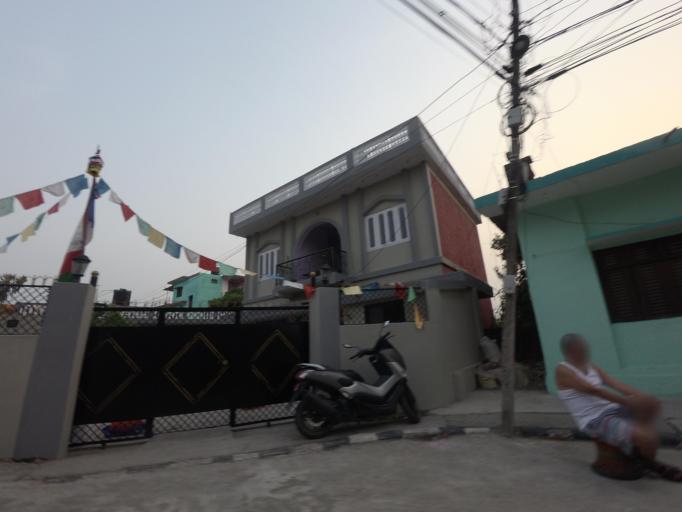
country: NP
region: Western Region
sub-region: Lumbini Zone
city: Bhairahawa
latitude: 27.5047
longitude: 83.4610
